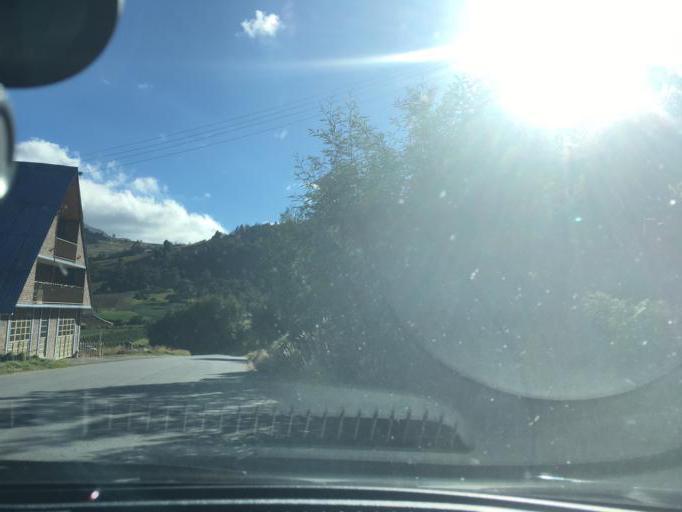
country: CO
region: Boyaca
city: Pesca
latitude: 5.5157
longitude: -72.9758
